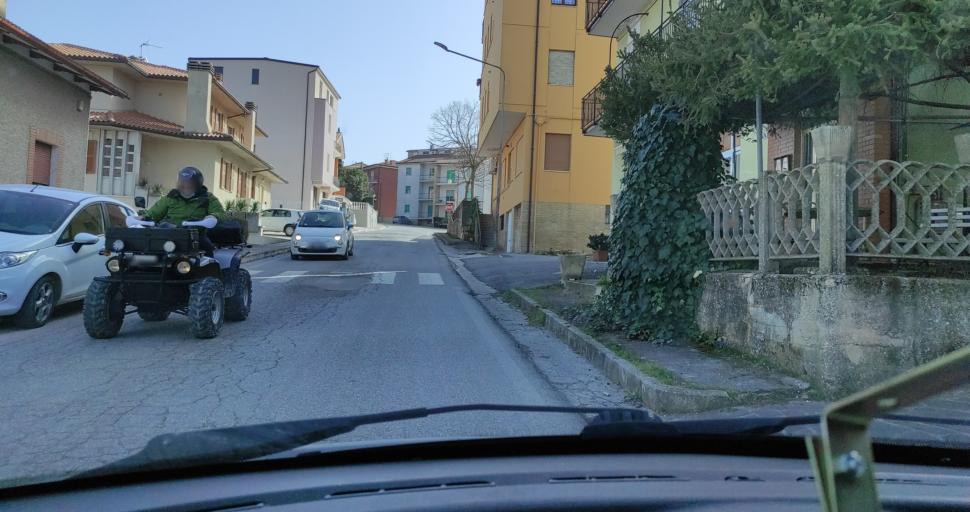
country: IT
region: The Marches
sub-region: Provincia di Macerata
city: Loro Piceno
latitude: 43.1645
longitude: 13.4090
